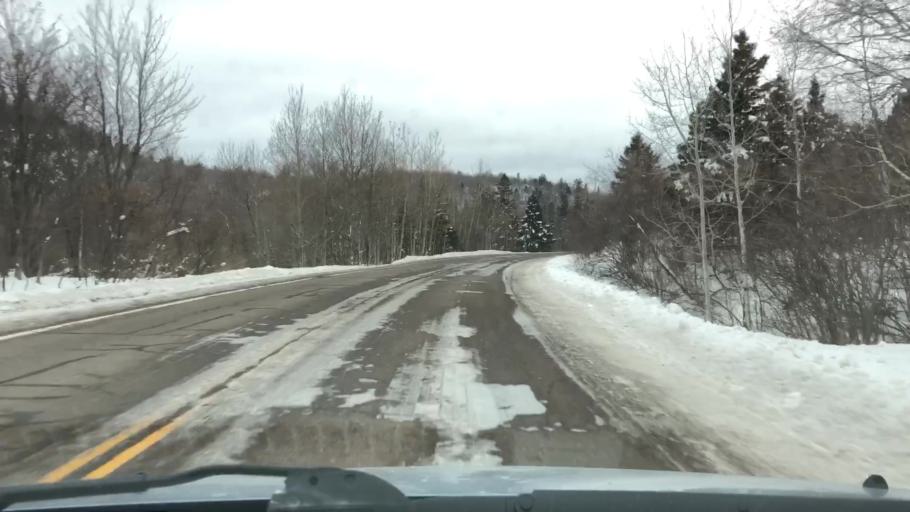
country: US
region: Minnesota
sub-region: Saint Louis County
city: Proctor
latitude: 46.7108
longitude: -92.2624
